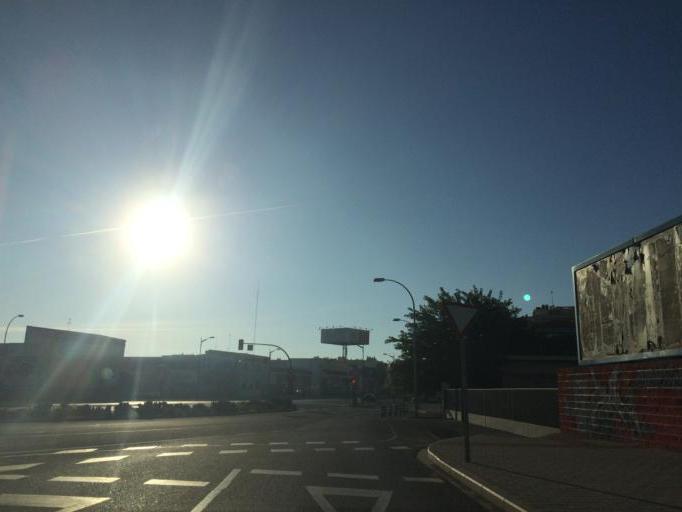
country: ES
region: Castille-La Mancha
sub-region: Provincia de Albacete
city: Albacete
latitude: 39.0099
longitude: -1.8737
